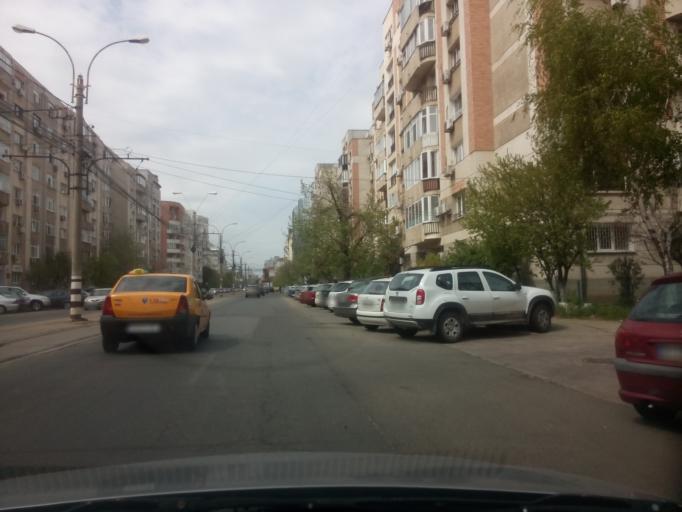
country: RO
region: Bucuresti
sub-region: Municipiul Bucuresti
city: Bucharest
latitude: 44.4322
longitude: 26.1278
